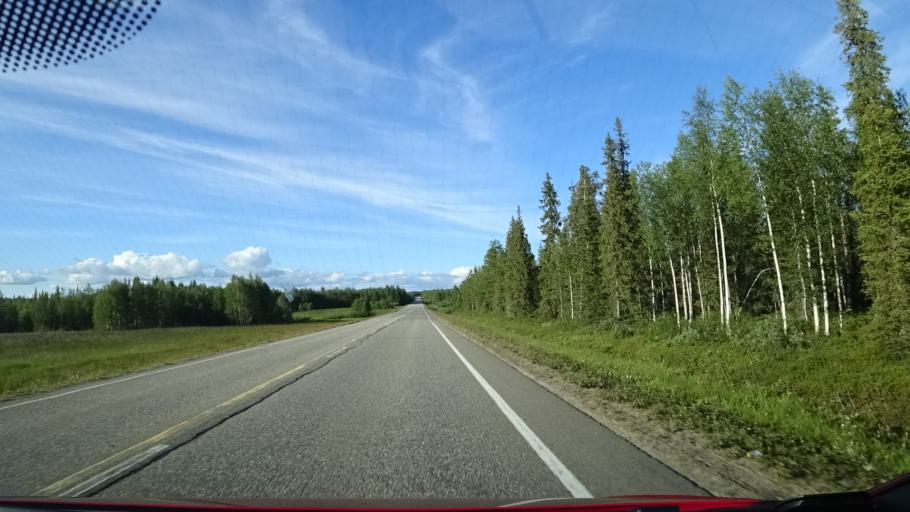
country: FI
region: Lapland
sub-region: Pohjois-Lappi
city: Sodankylae
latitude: 67.9548
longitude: 26.7803
